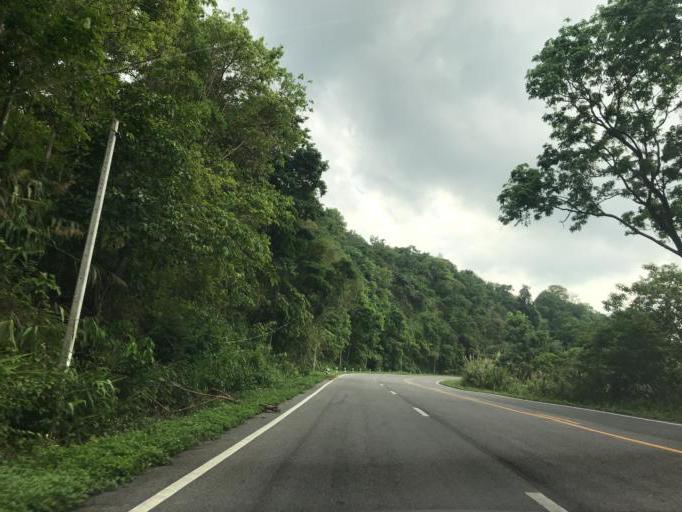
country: TH
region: Phayao
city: Phayao
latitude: 19.0720
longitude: 99.8137
